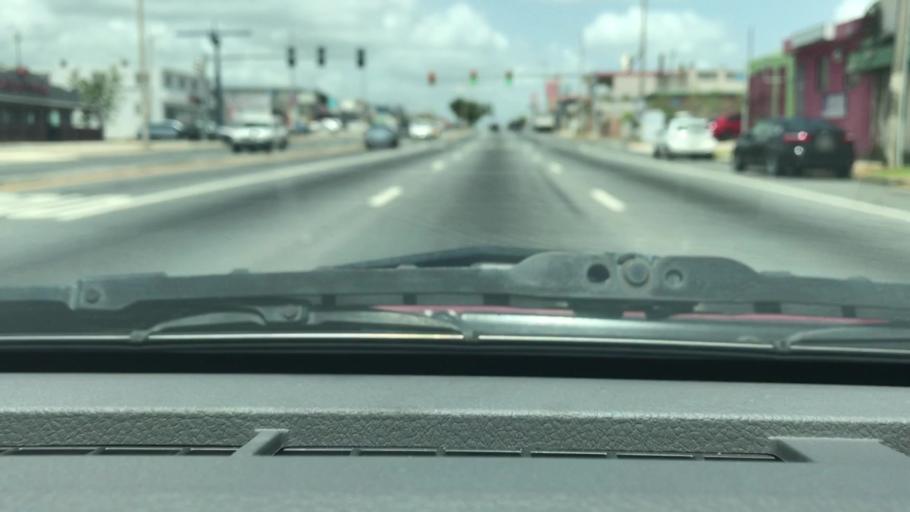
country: PR
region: Bayamon
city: Bayamon
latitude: 18.3658
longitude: -66.1718
